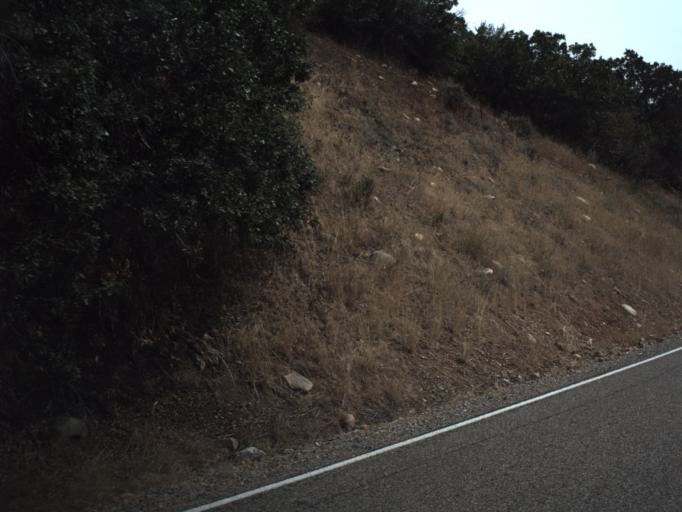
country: US
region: Utah
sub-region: Summit County
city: Summit Park
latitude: 40.8527
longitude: -111.6064
